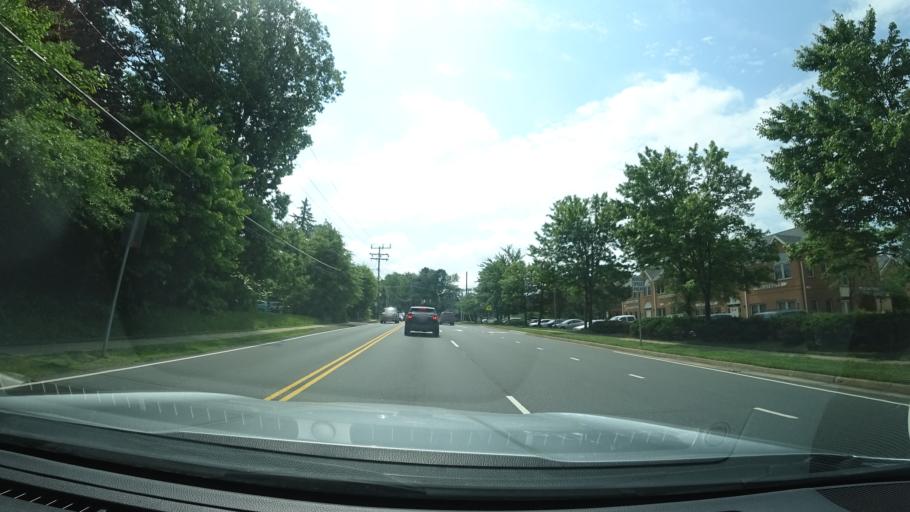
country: US
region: Virginia
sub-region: Fairfax County
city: Herndon
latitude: 38.9690
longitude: -77.3961
